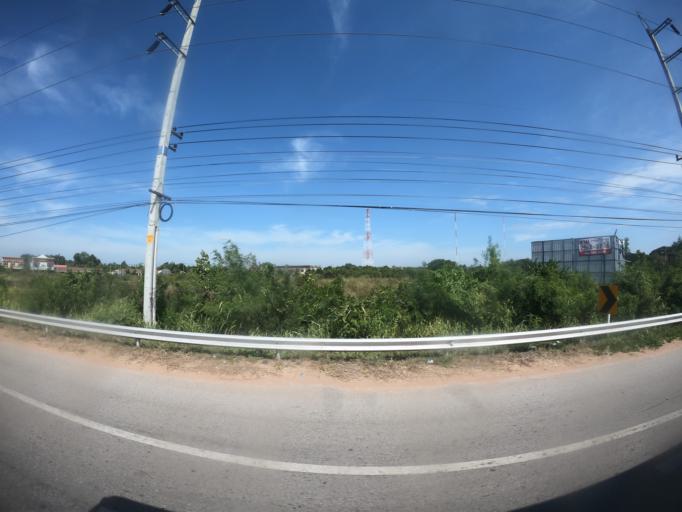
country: TH
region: Khon Kaen
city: Khon Kaen
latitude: 16.4465
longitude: 102.9493
